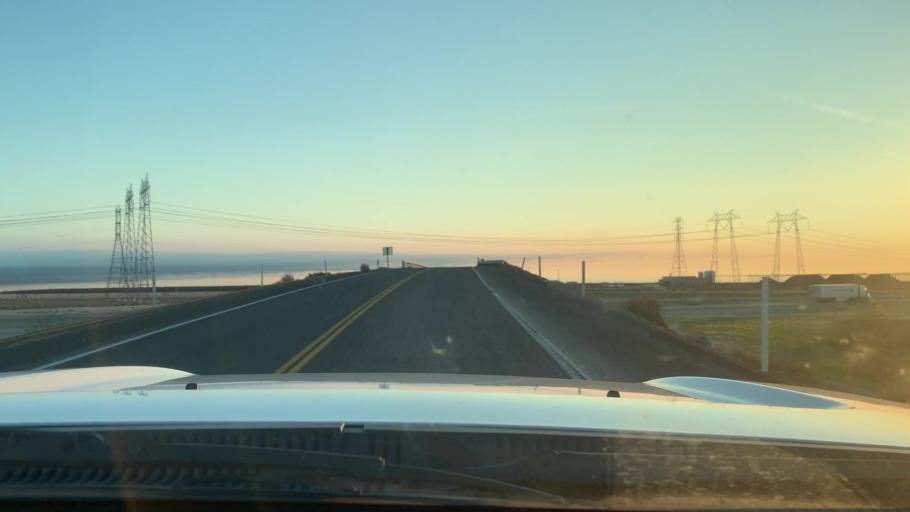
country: US
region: California
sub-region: Kern County
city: Buttonwillow
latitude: 35.4998
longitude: -119.5363
